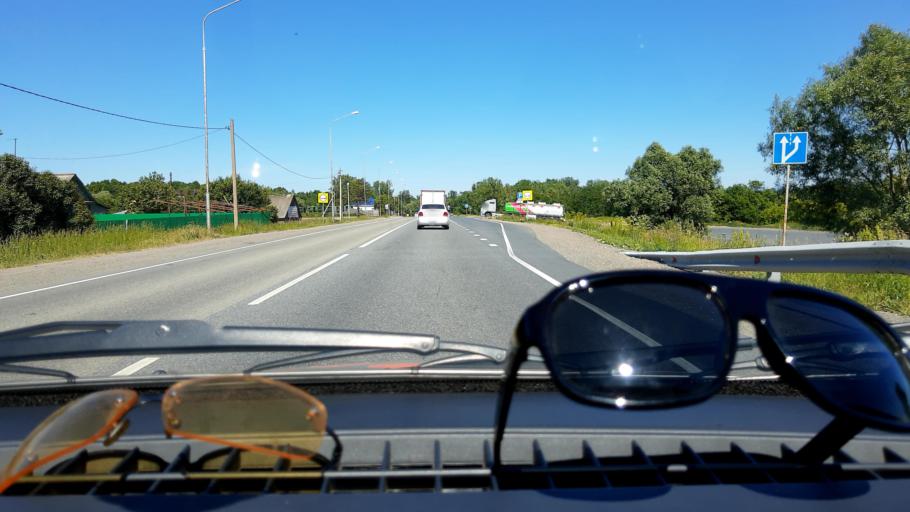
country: RU
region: Bashkortostan
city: Urman
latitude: 54.8233
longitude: 56.8875
